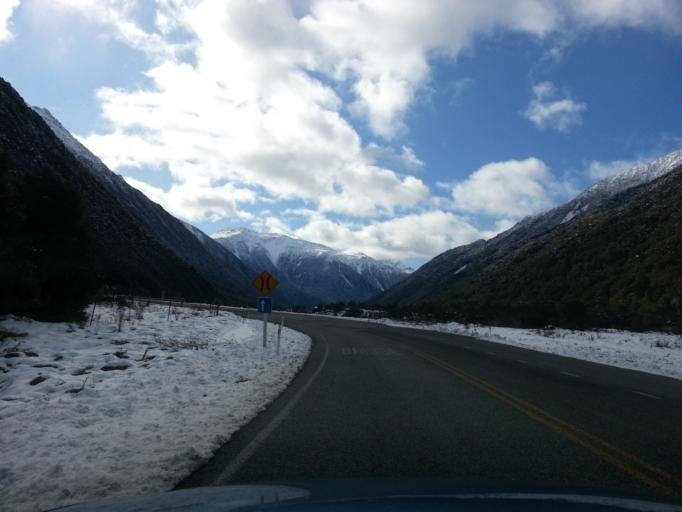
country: NZ
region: West Coast
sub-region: Grey District
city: Greymouth
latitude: -42.8530
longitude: 171.5608
